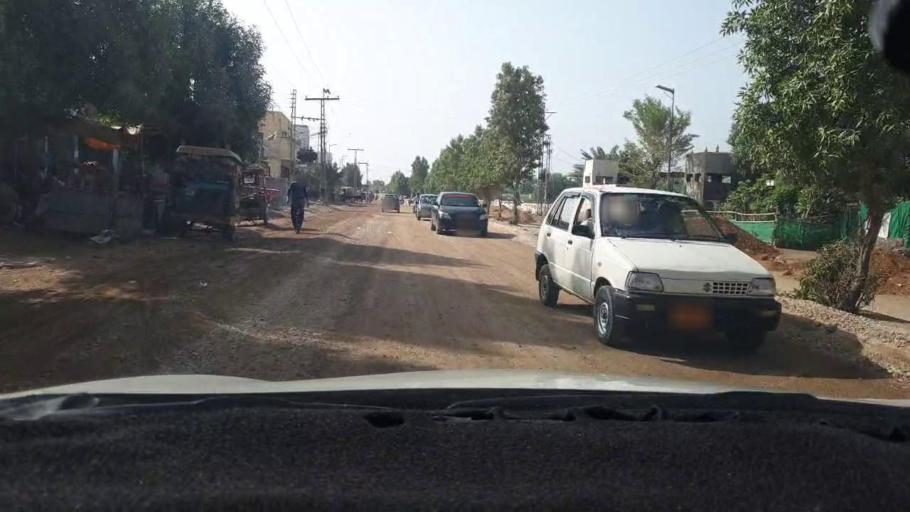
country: PK
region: Sindh
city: Sanghar
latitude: 26.0408
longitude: 68.9501
